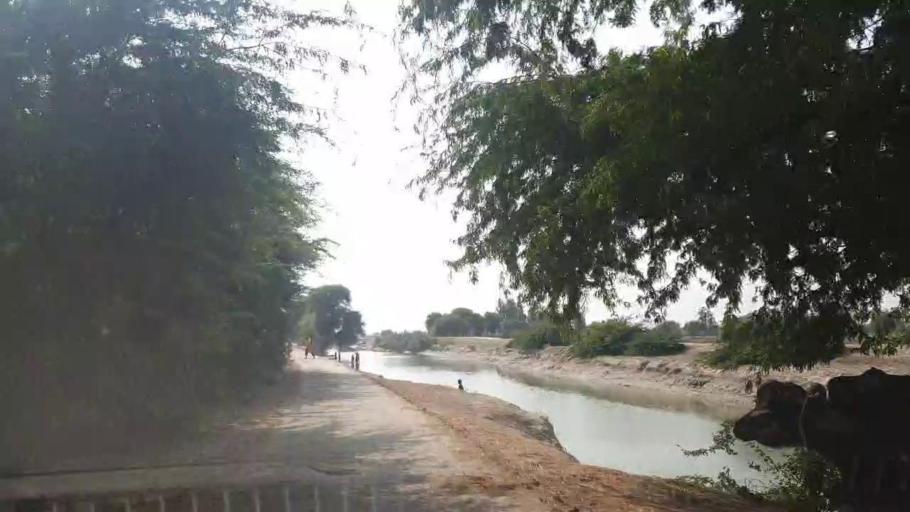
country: PK
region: Sindh
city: Badin
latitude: 24.7369
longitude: 68.7353
